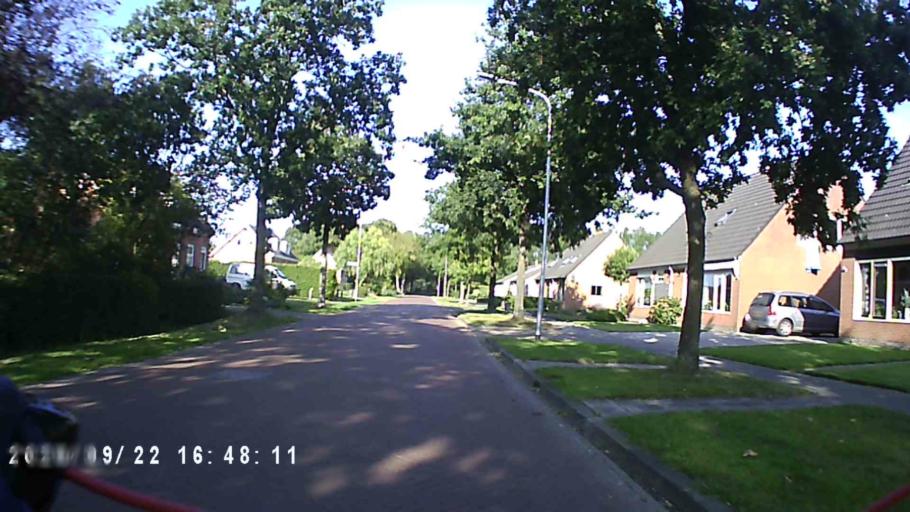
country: NL
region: Groningen
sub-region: Gemeente Leek
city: Leek
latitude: 53.1333
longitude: 6.4785
